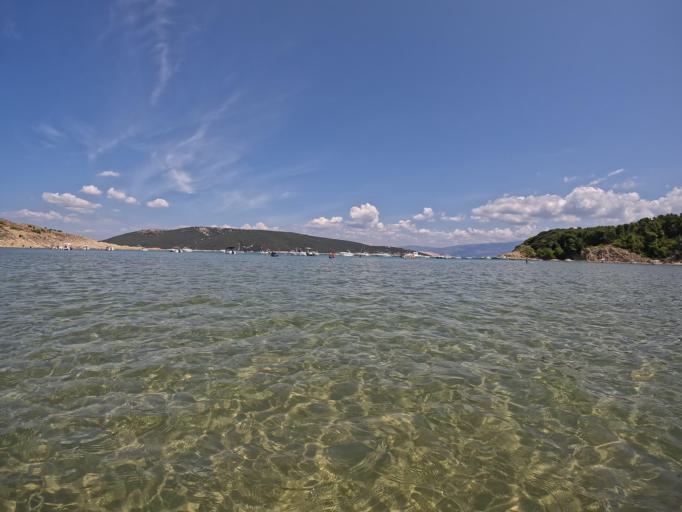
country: HR
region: Primorsko-Goranska
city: Lopar
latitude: 44.8393
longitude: 14.7535
